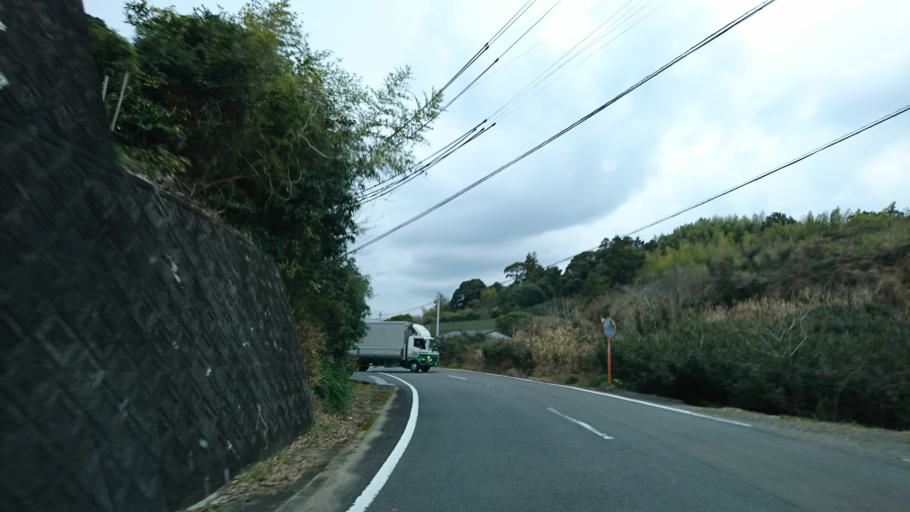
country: JP
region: Shizuoka
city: Sagara
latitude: 34.7396
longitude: 138.1801
